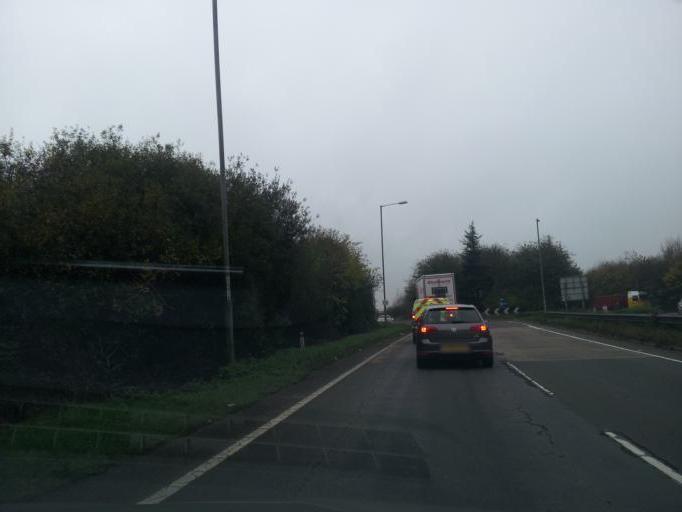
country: GB
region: England
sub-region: Northamptonshire
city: Brackley
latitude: 52.0270
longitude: -1.1335
